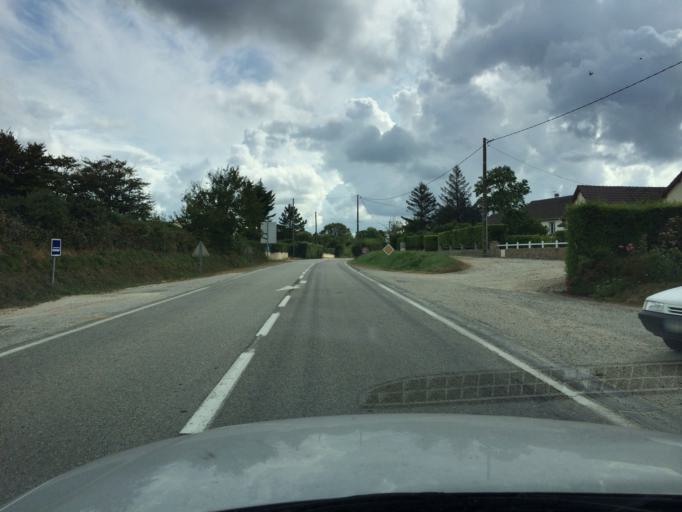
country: FR
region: Lower Normandy
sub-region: Departement de la Manche
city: Brix
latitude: 49.5635
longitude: -1.5899
